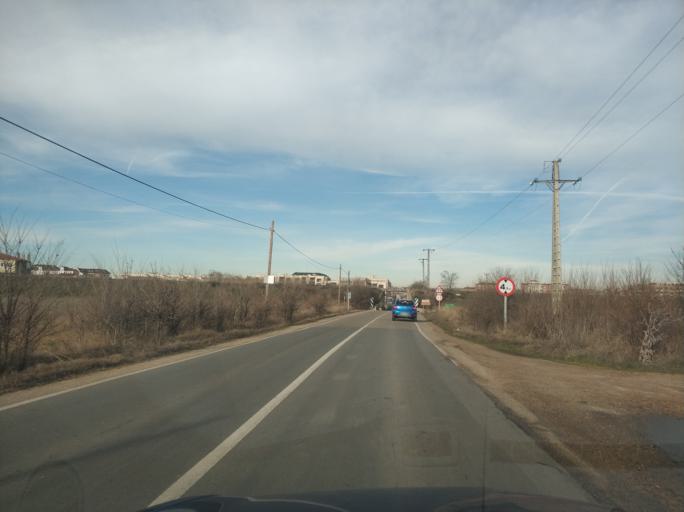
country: ES
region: Castille and Leon
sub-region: Provincia de Zamora
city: Zamora
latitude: 41.4930
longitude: -5.7364
